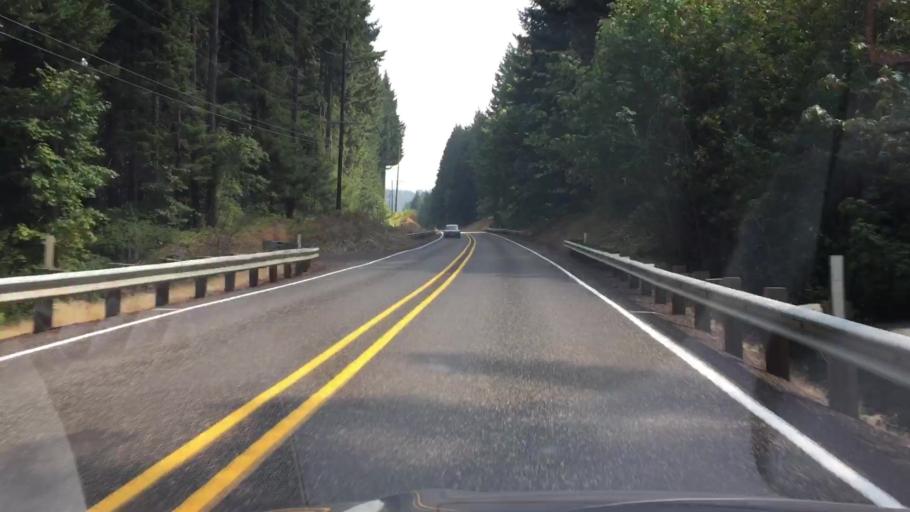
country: US
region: Washington
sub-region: Klickitat County
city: White Salmon
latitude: 45.8767
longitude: -121.5195
